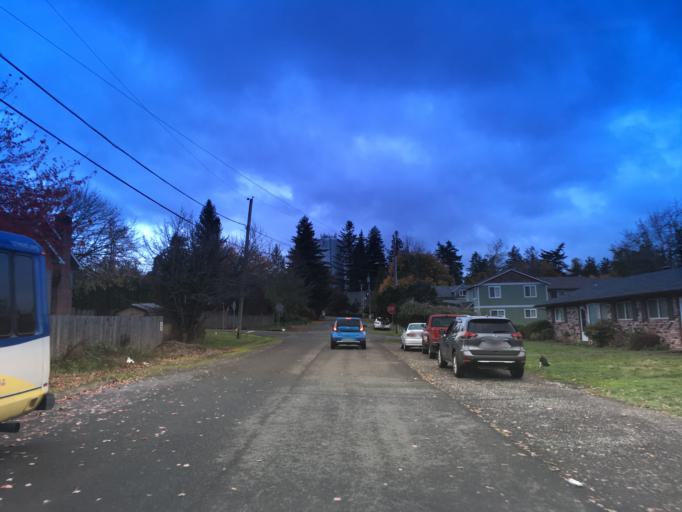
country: US
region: Oregon
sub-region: Multnomah County
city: Fairview
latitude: 45.5353
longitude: -122.4381
